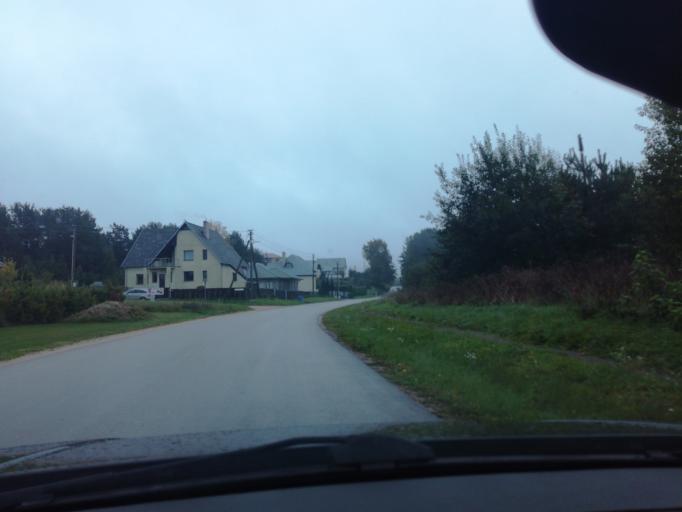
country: LT
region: Alytaus apskritis
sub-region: Alytus
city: Alytus
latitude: 54.3982
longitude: 24.0860
